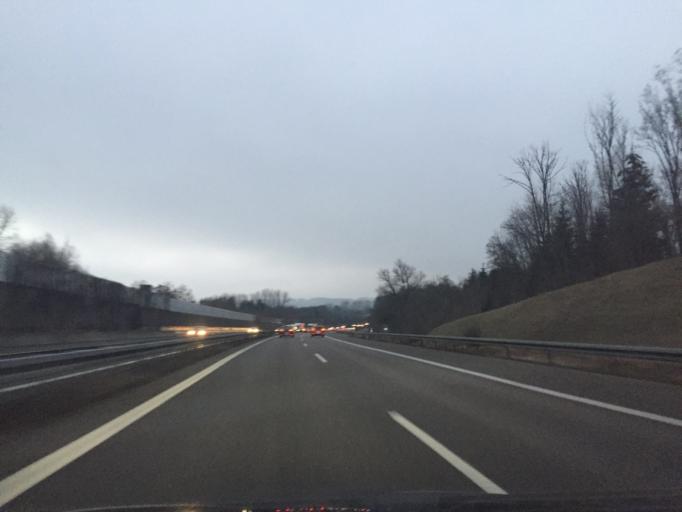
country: DE
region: Bavaria
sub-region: Upper Bavaria
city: Greifenberg
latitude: 48.0711
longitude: 11.0653
